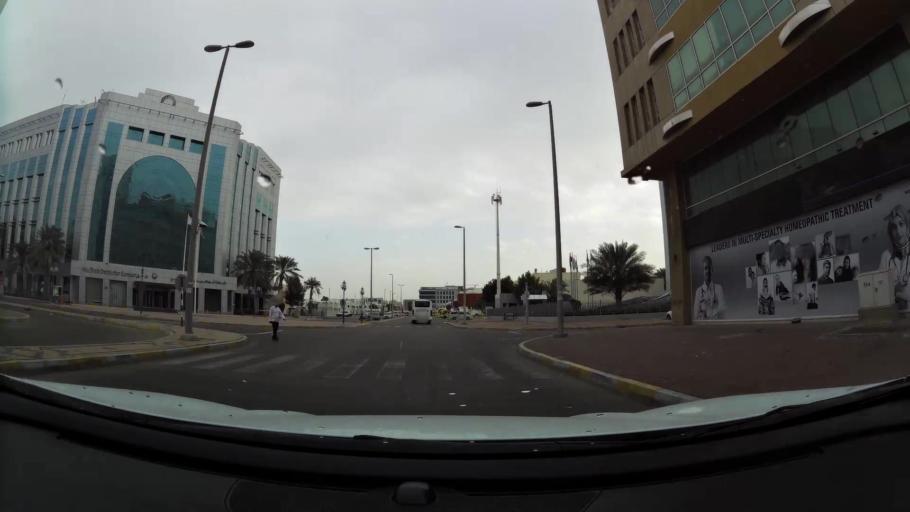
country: AE
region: Abu Dhabi
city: Abu Dhabi
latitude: 24.4837
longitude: 54.3776
